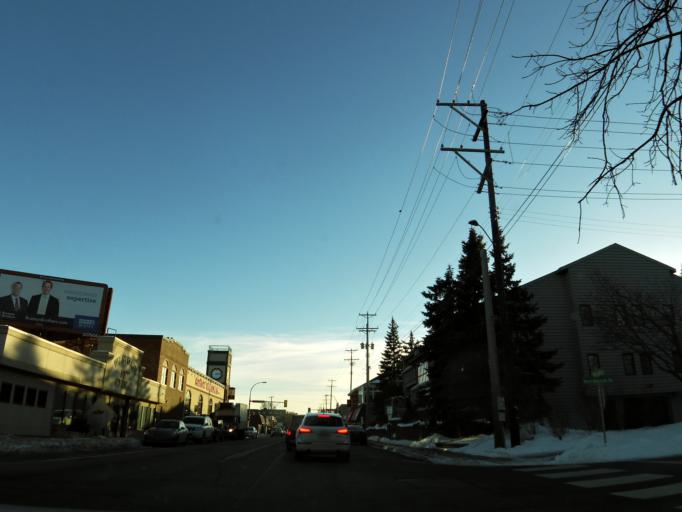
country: US
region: Minnesota
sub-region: Hennepin County
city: Saint Louis Park
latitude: 44.9234
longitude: -93.3292
